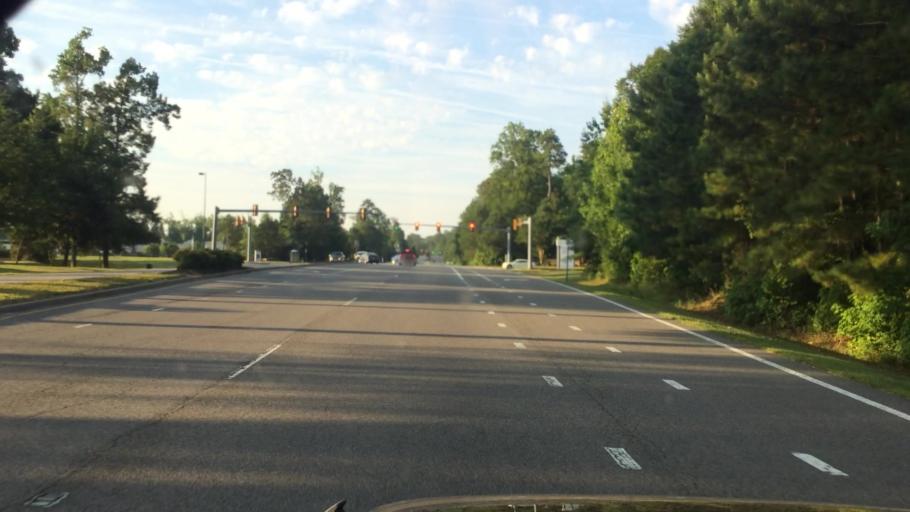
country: US
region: Virginia
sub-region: James City County
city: Williamsburg
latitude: 37.3404
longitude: -76.7388
